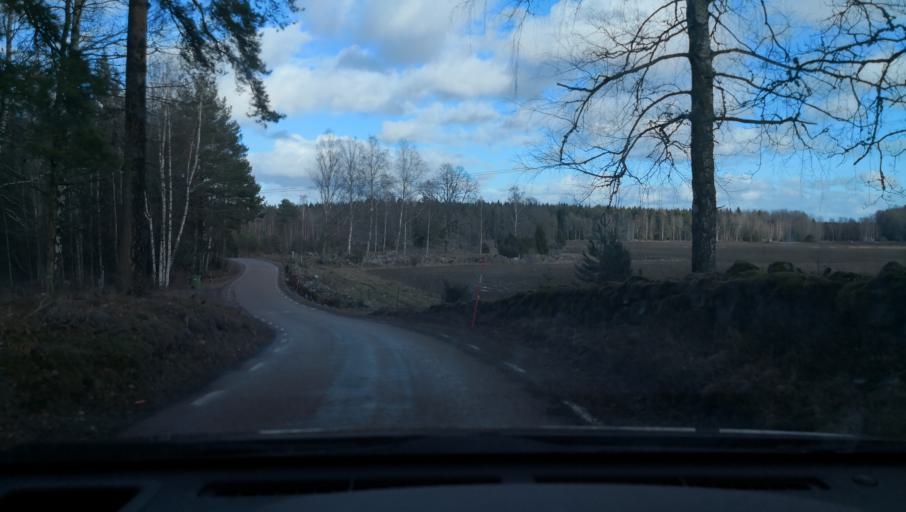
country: SE
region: Vaestmanland
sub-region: Arboga Kommun
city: Arboga
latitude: 59.3173
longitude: 15.7706
